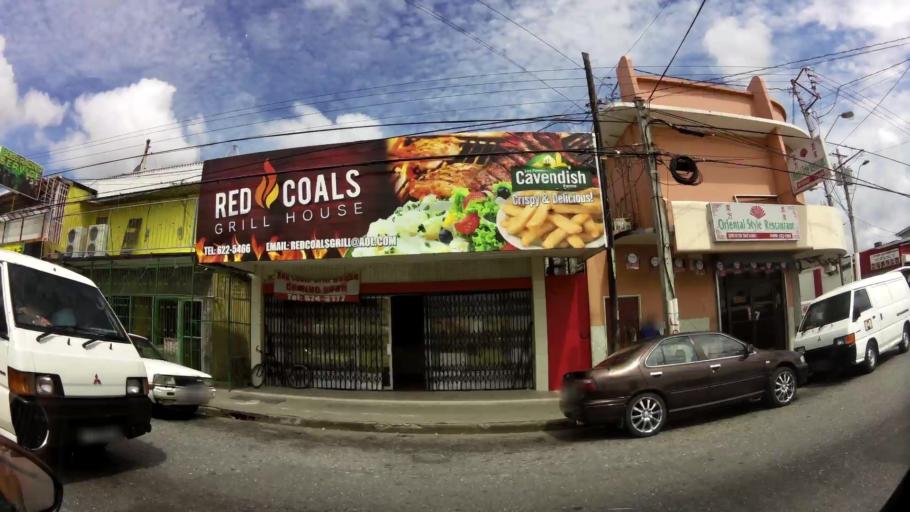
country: TT
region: City of Port of Spain
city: Mucurapo
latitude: 10.6718
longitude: -61.5332
